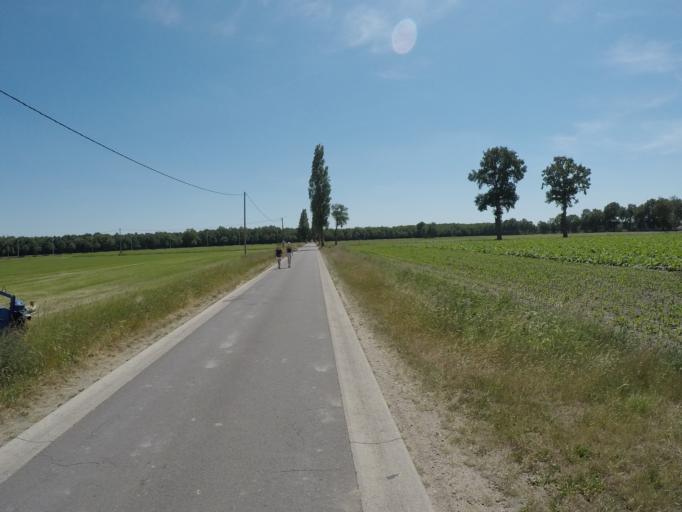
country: BE
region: Flanders
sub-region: Provincie Antwerpen
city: Wuustwezel
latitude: 51.3733
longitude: 4.5645
